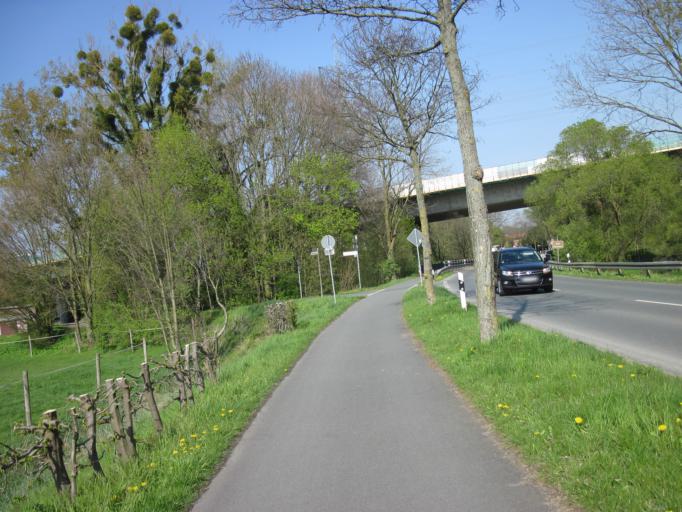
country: DE
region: North Rhine-Westphalia
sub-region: Regierungsbezirk Detmold
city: Paderborn
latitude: 51.6949
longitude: 8.7071
